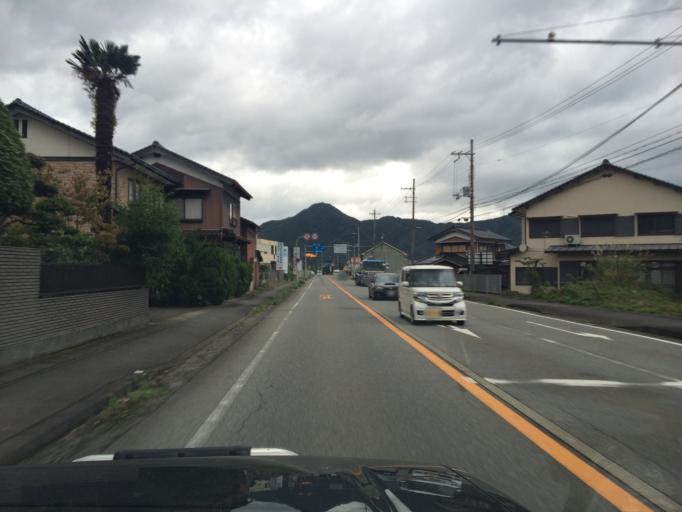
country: JP
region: Hyogo
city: Toyooka
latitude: 35.4210
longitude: 134.7906
